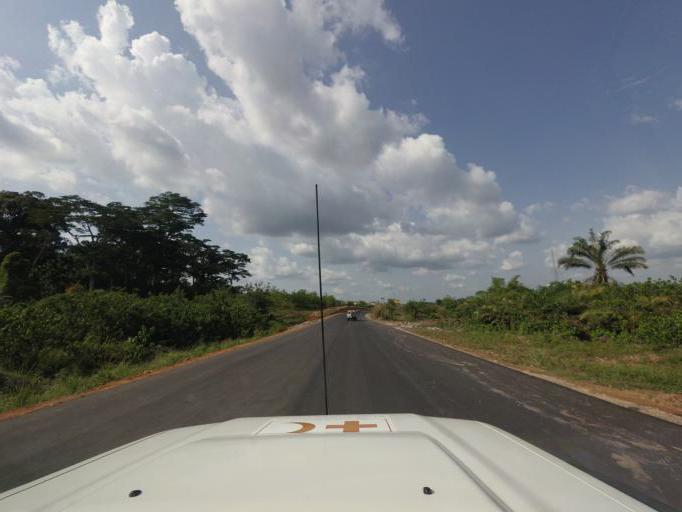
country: LR
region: Bong
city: Gbarnga
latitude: 6.9992
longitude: -9.5709
